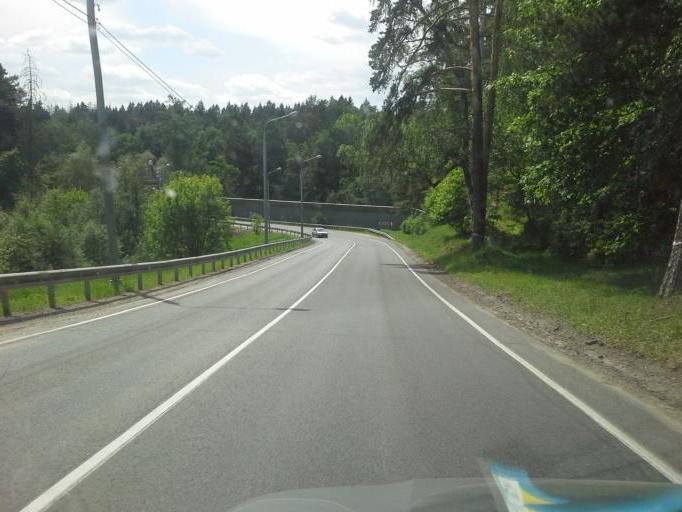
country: RU
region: Moskovskaya
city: Barvikha
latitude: 55.7191
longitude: 37.2665
